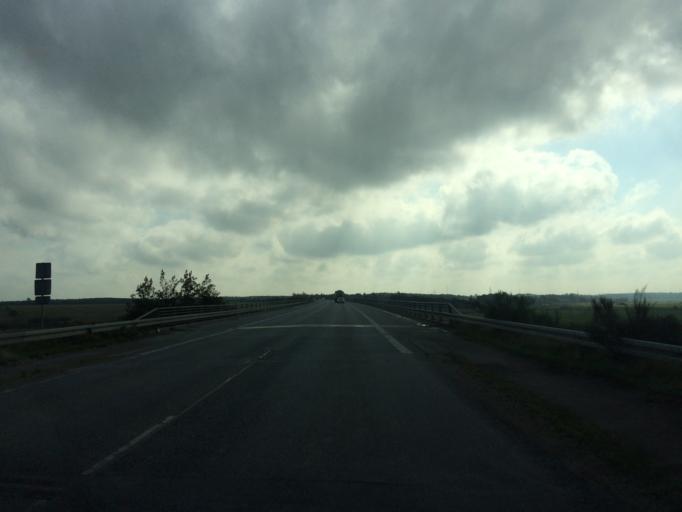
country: DK
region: Central Jutland
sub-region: Skive Kommune
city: Skive
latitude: 56.5473
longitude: 8.9937
